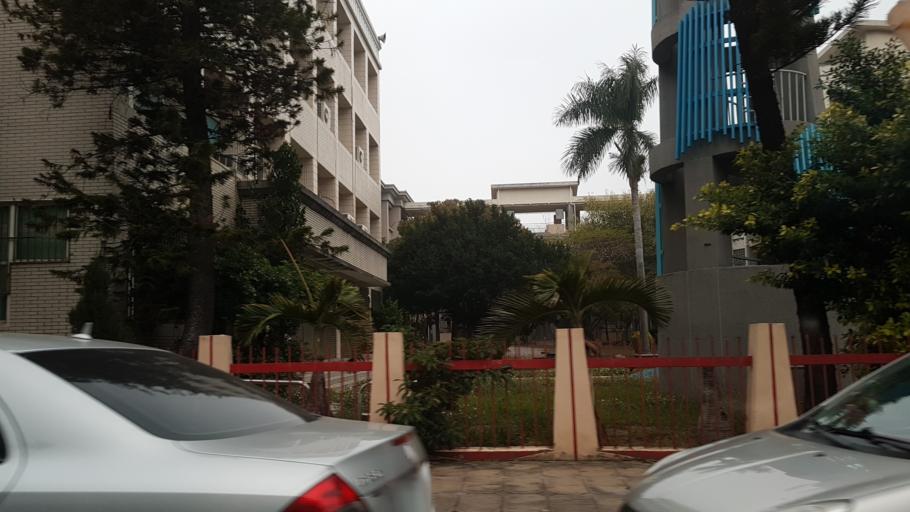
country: TW
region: Taiwan
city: Xinying
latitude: 23.3093
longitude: 120.3120
